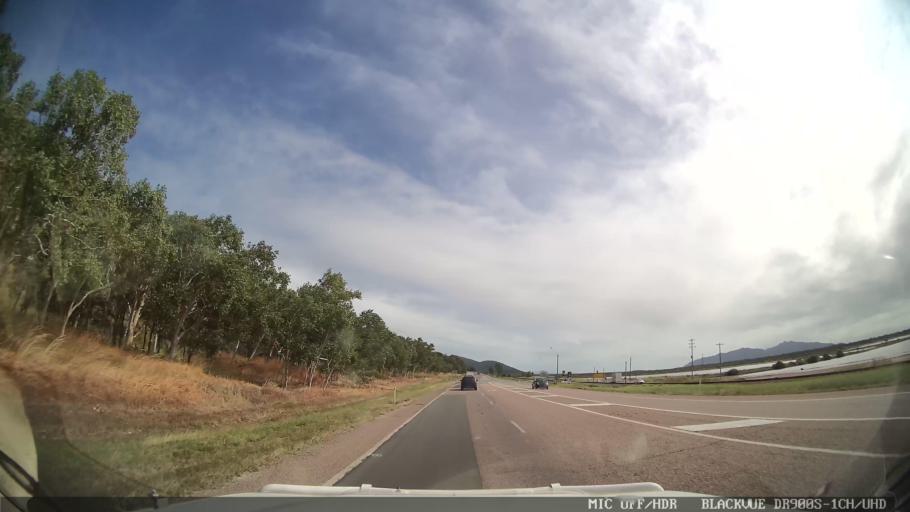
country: AU
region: Queensland
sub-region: Townsville
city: Townsville
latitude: -19.3975
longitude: 147.0224
